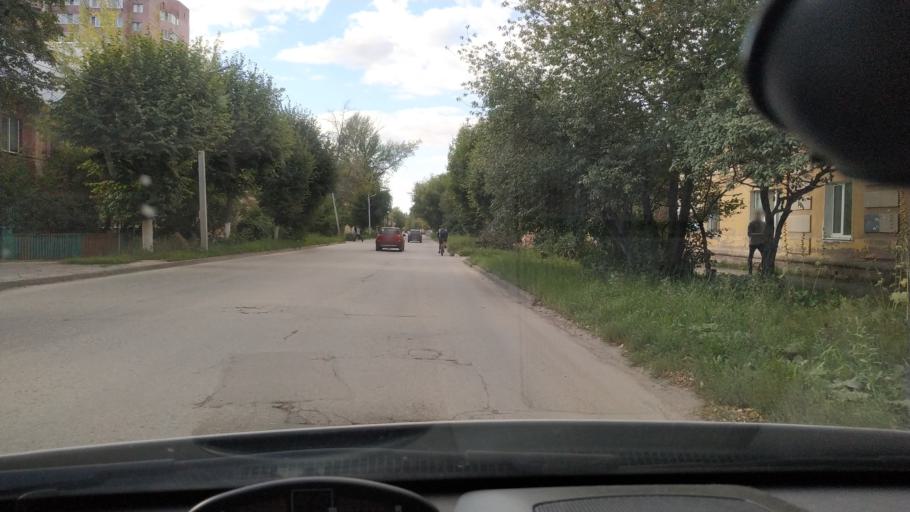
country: RU
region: Rjazan
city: Ryazan'
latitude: 54.6196
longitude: 39.7072
